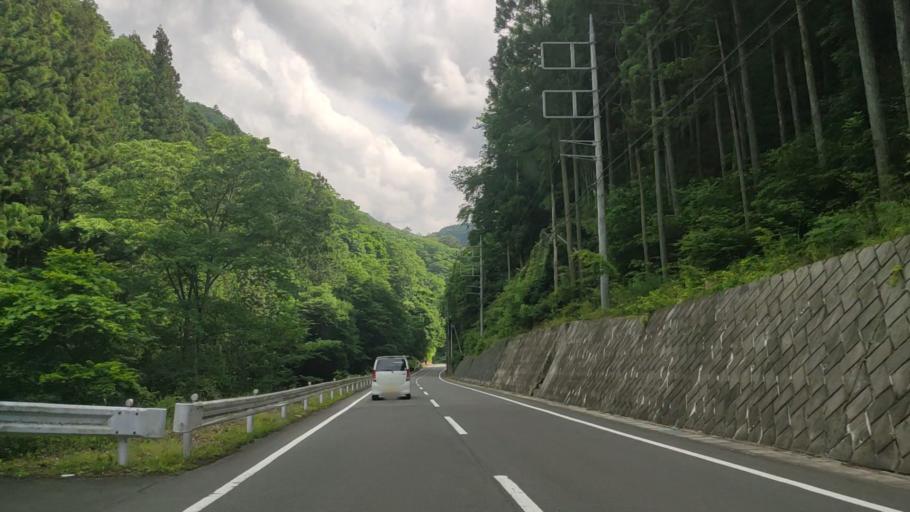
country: JP
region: Gunma
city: Tomioka
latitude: 36.0972
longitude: 138.7170
